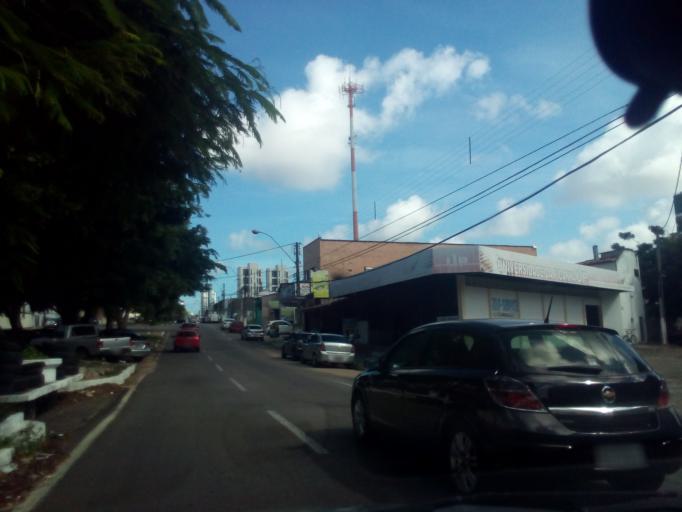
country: BR
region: Rio Grande do Norte
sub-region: Natal
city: Natal
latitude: -5.8014
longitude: -35.2116
